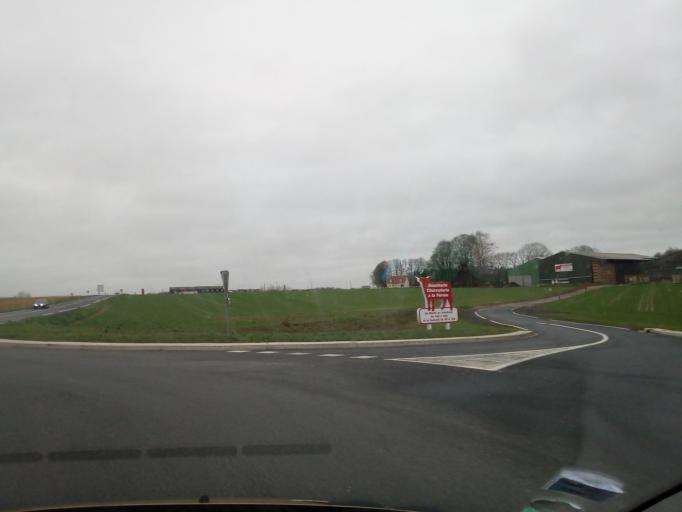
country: FR
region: Haute-Normandie
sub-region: Departement de la Seine-Maritime
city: Auzebosc
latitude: 49.5981
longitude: 0.7377
